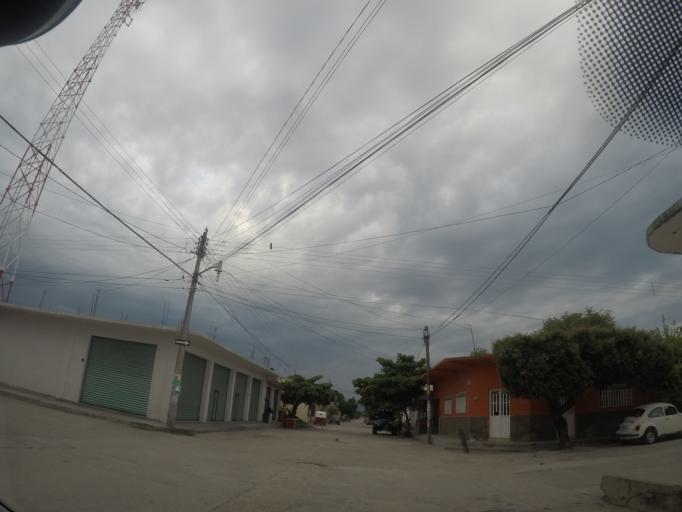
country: MX
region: Oaxaca
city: Chahuite
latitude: 16.2893
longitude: -94.1948
